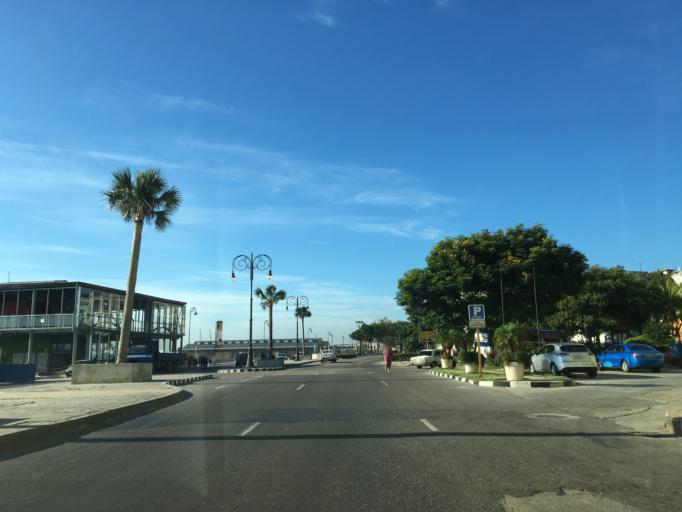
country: CU
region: La Habana
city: La Habana Vieja
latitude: 23.1345
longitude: -82.3474
